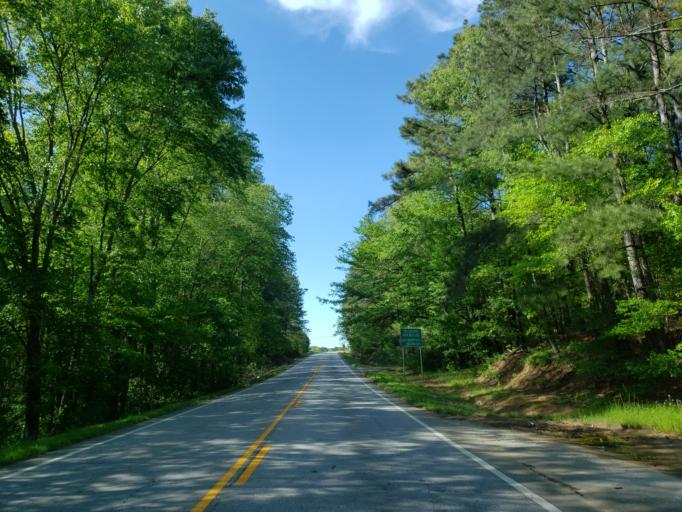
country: US
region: Georgia
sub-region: Haralson County
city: Tallapoosa
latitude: 33.7282
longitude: -85.2818
